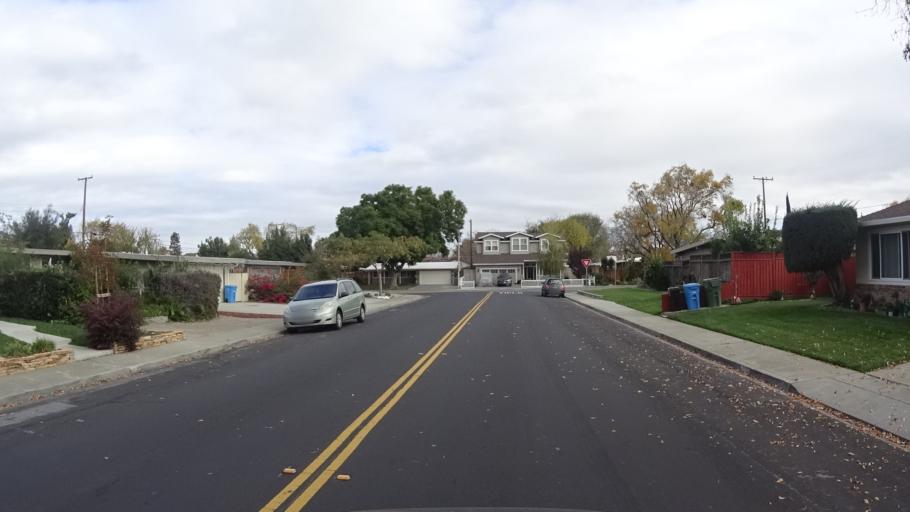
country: US
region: California
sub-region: Santa Clara County
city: Cupertino
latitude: 37.3247
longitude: -121.9923
